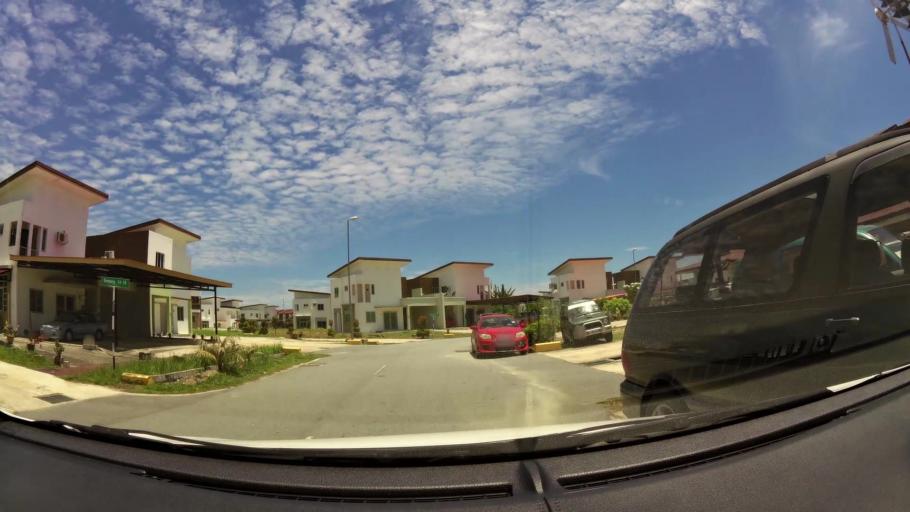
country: BN
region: Brunei and Muara
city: Bandar Seri Begawan
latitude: 5.0046
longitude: 115.0089
